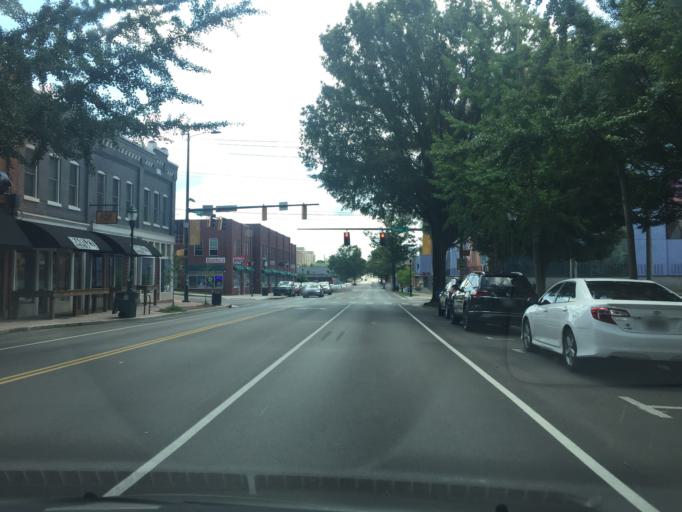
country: US
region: Tennessee
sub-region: Hamilton County
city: Chattanooga
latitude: 35.0450
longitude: -85.3062
